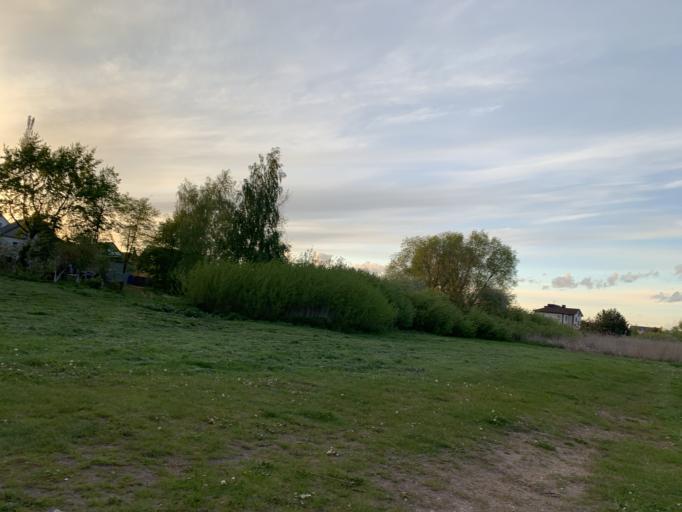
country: BY
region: Minsk
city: Nyasvizh
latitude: 53.2093
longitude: 26.6661
